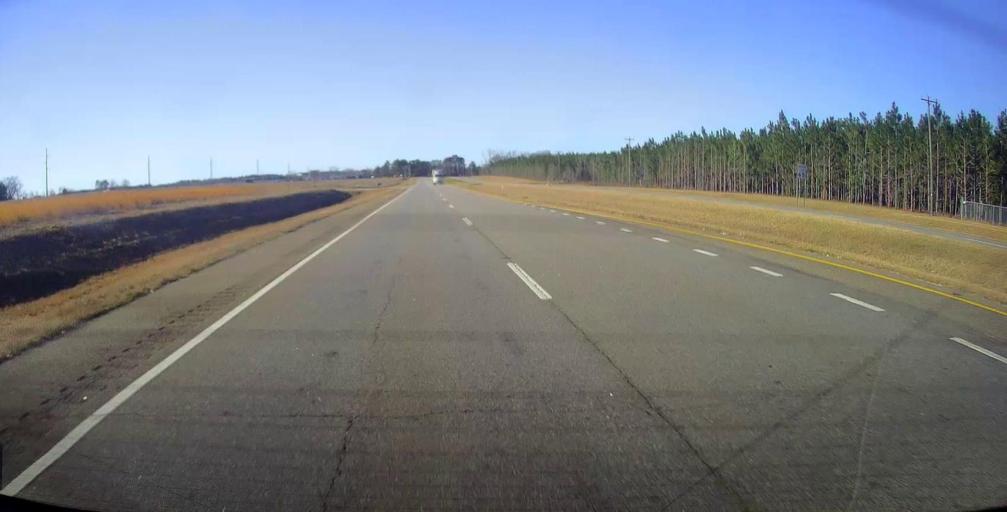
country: US
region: Georgia
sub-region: Sumter County
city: Americus
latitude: 31.9185
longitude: -84.2622
